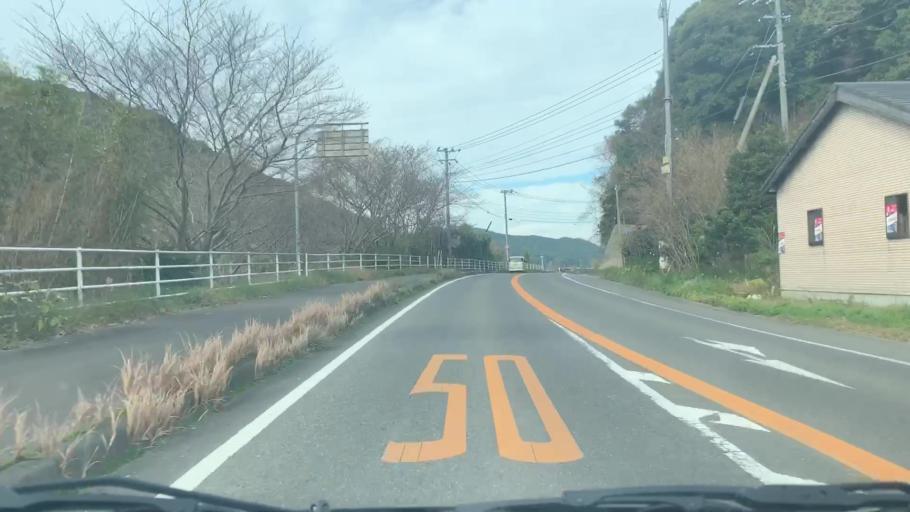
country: JP
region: Saga Prefecture
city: Karatsu
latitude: 33.3640
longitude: 130.0080
